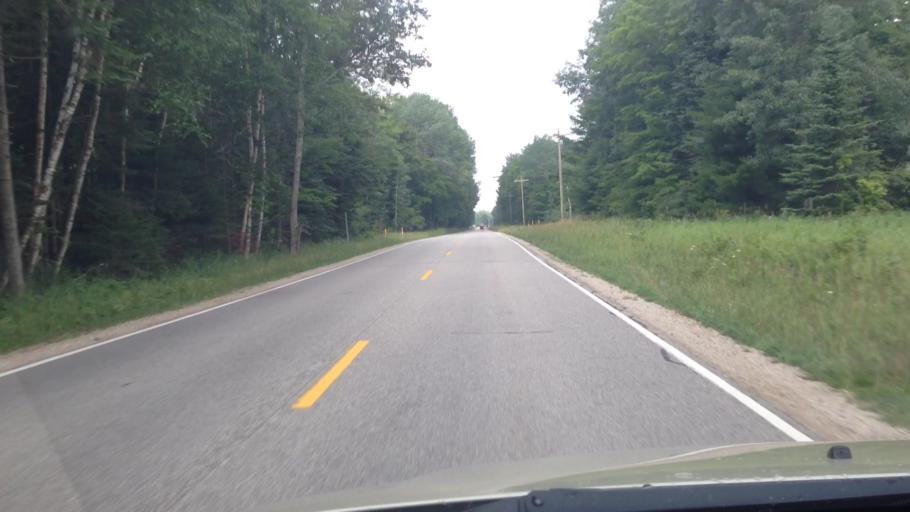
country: US
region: Michigan
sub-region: Mackinac County
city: Saint Ignace
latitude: 46.0569
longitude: -85.1399
